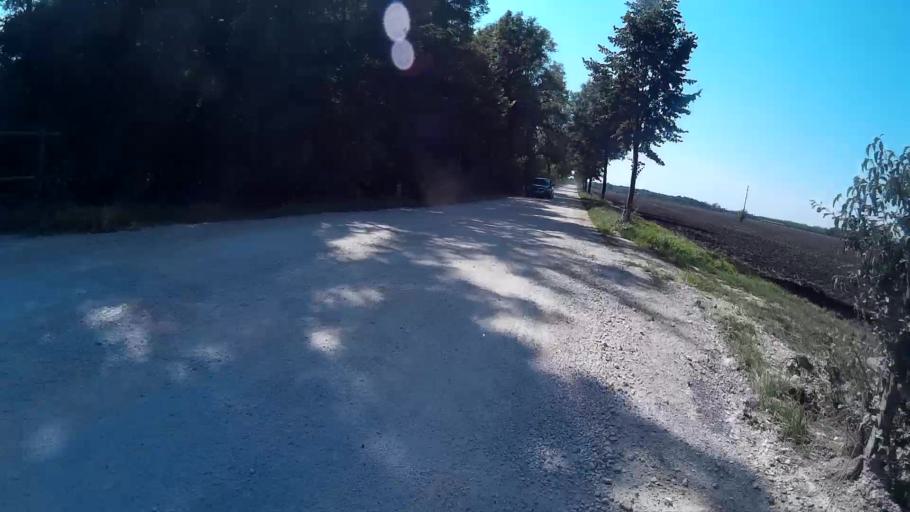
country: CZ
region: South Moravian
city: Novosedly
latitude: 48.7964
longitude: 16.4908
